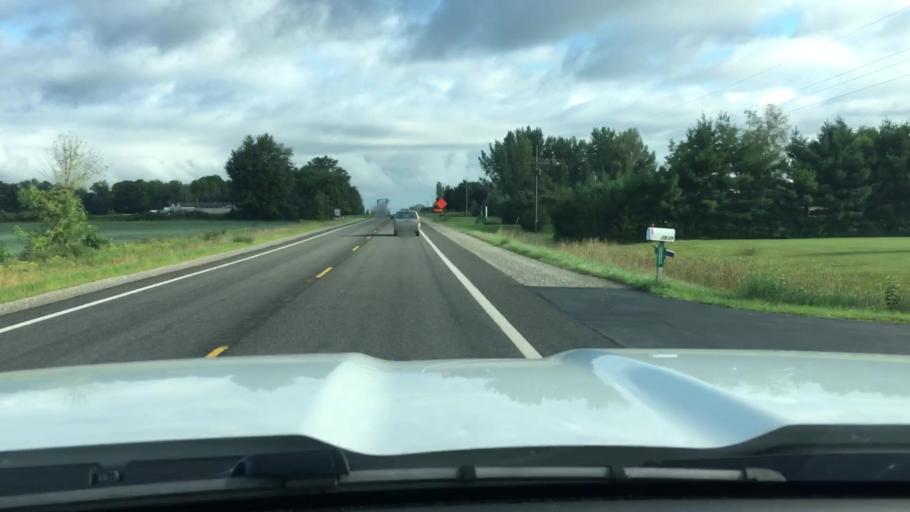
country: US
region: Michigan
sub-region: Tuscola County
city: Caro
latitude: 43.3961
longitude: -83.3835
